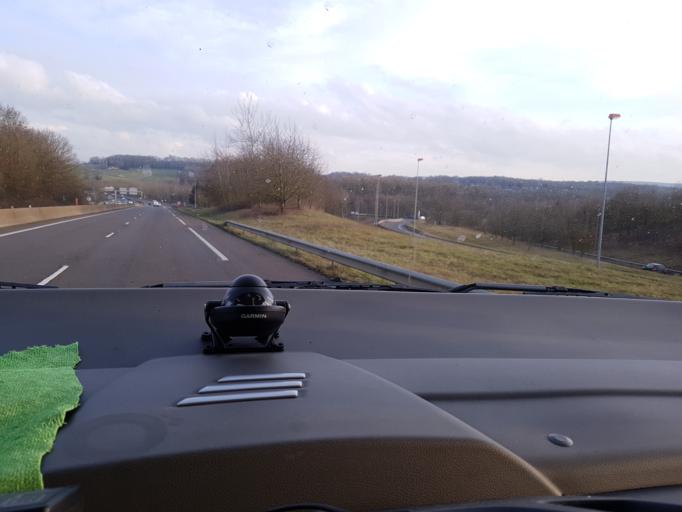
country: FR
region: Champagne-Ardenne
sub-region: Departement des Ardennes
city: La Francheville
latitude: 49.7364
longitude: 4.7175
